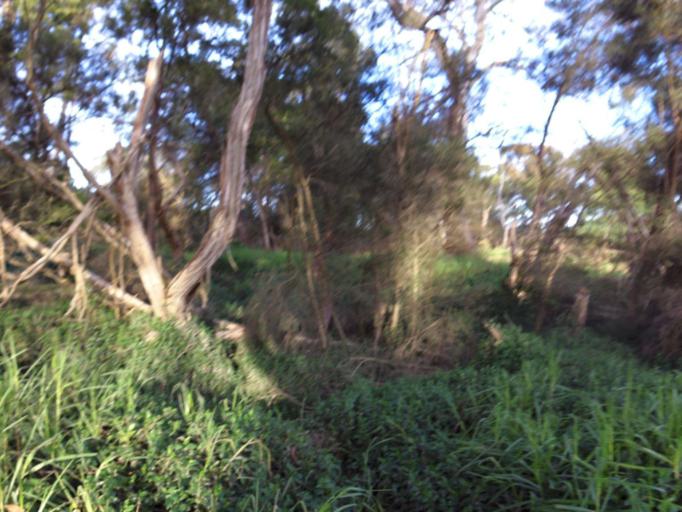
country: AU
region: Victoria
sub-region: Knox
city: Wantirna
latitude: -37.8485
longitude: 145.2101
